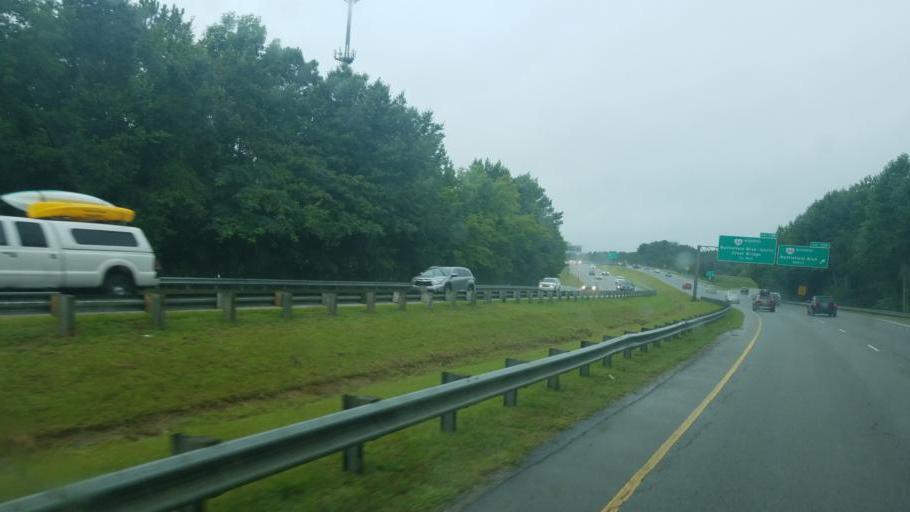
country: US
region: Virginia
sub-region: City of Chesapeake
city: Chesapeake
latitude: 36.7354
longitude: -76.2369
